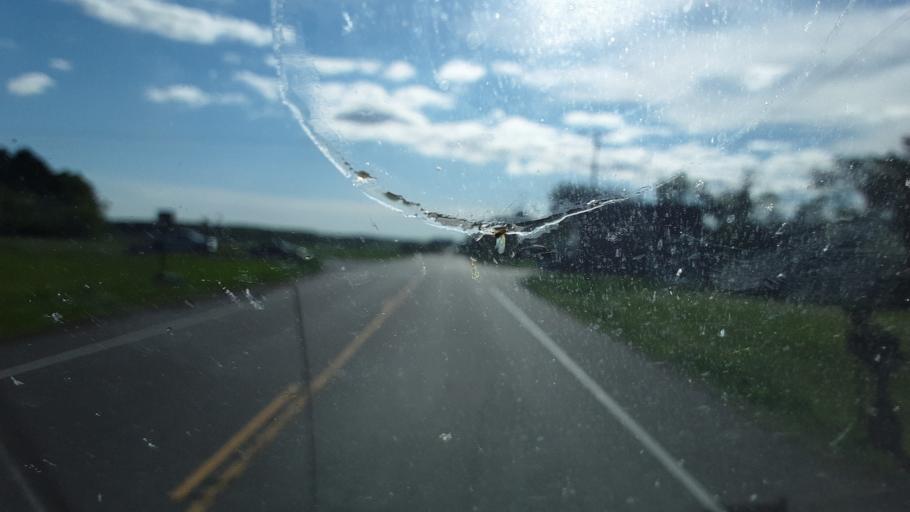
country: US
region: Wisconsin
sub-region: Marathon County
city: Spencer
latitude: 44.6562
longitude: -90.2986
